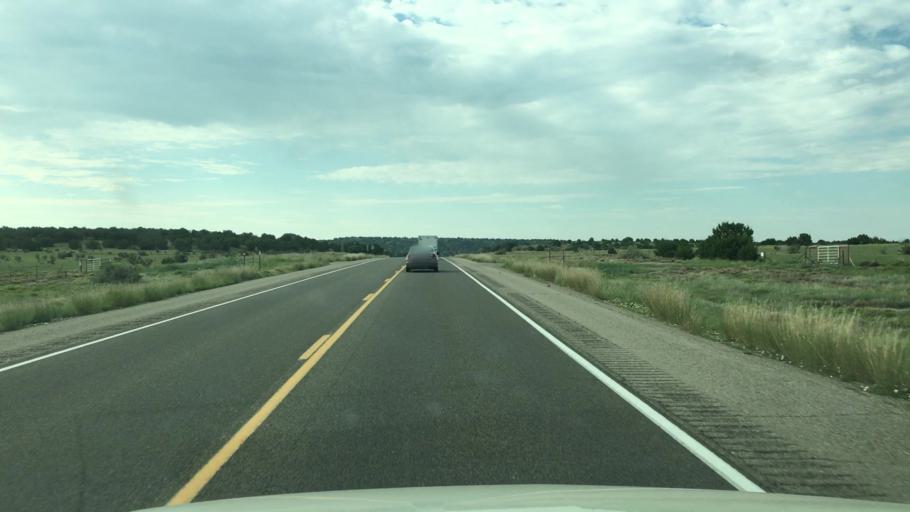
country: US
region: New Mexico
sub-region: Santa Fe County
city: Eldorado at Santa Fe
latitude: 35.2911
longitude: -105.8247
